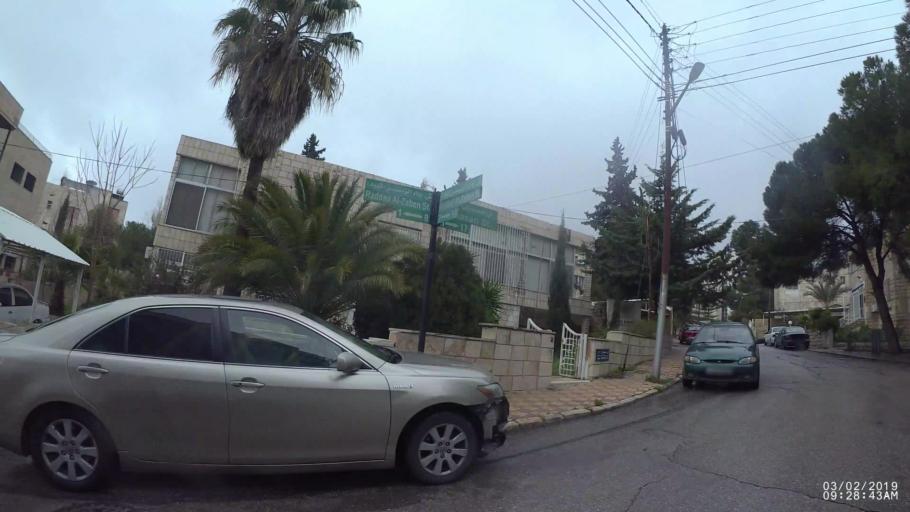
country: JO
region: Amman
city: Amman
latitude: 31.9491
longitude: 35.9066
